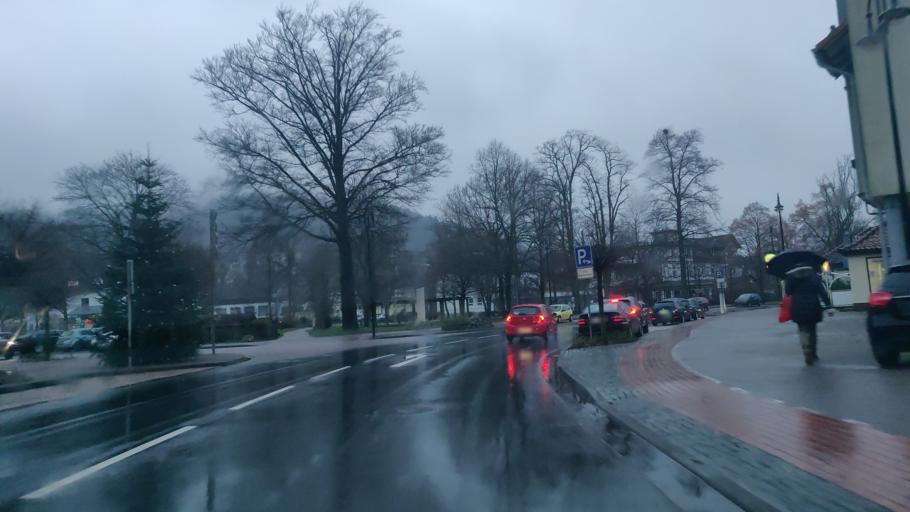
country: DE
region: Lower Saxony
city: Bad Lauterberg im Harz
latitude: 51.6311
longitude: 10.4705
